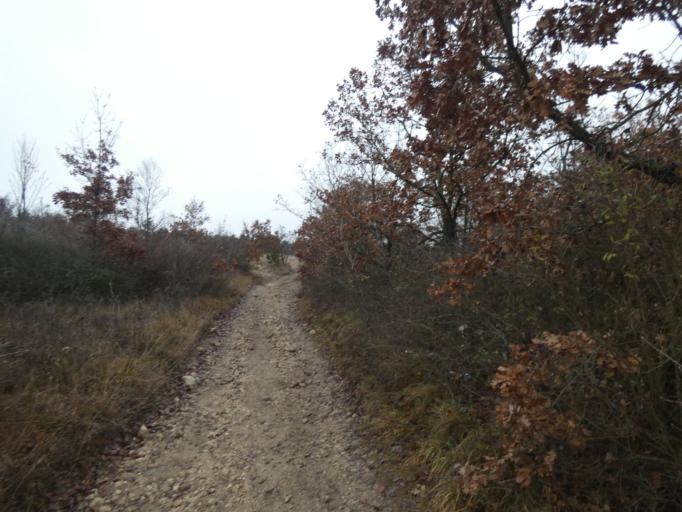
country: HU
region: Pest
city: Soskut
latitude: 47.4285
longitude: 18.8463
